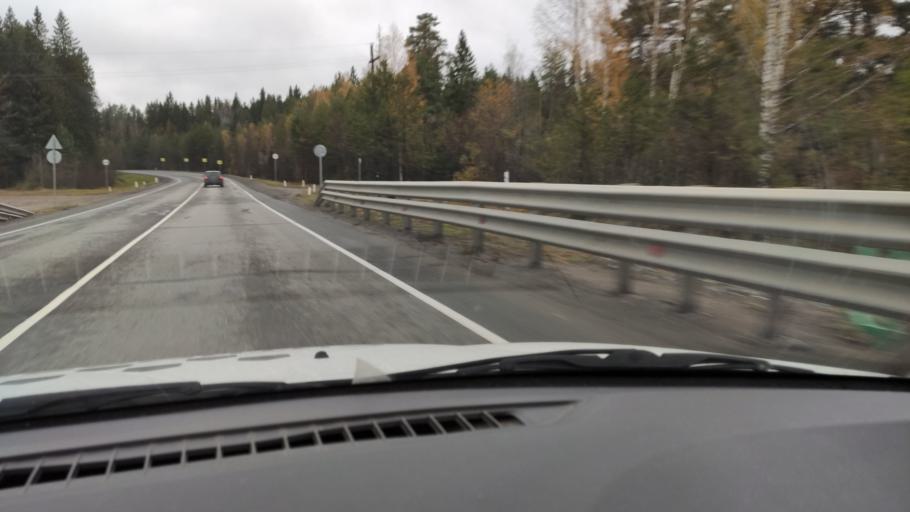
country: RU
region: Kirov
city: Belaya Kholunitsa
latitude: 58.9050
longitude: 50.9447
